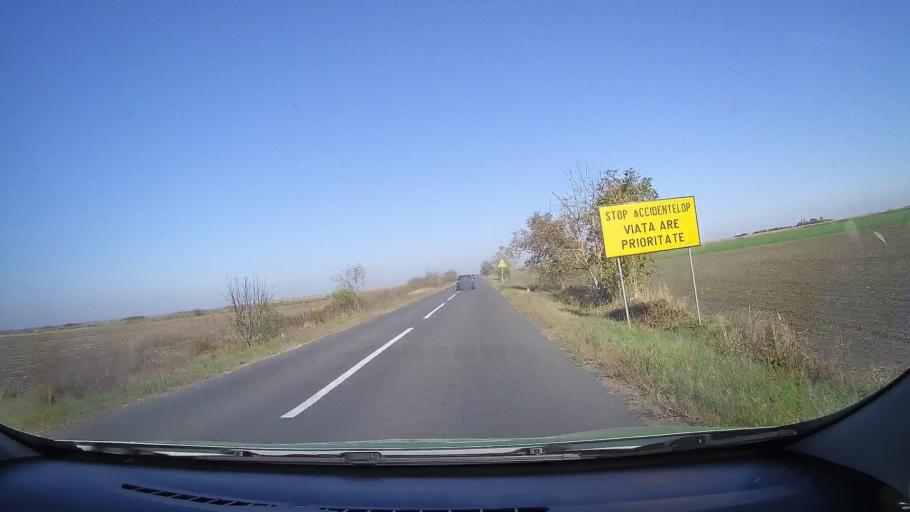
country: RO
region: Satu Mare
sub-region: Comuna Cauas
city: Cauas
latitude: 47.6014
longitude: 22.5453
